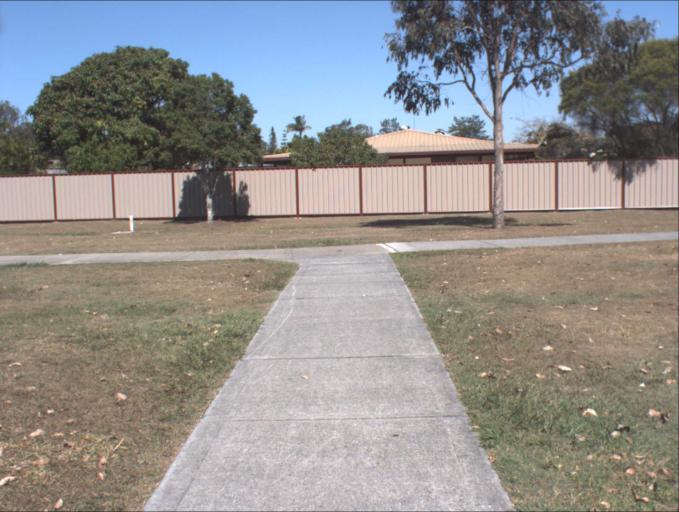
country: AU
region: Queensland
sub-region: Gold Coast
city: Yatala
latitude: -27.7089
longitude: 153.2247
